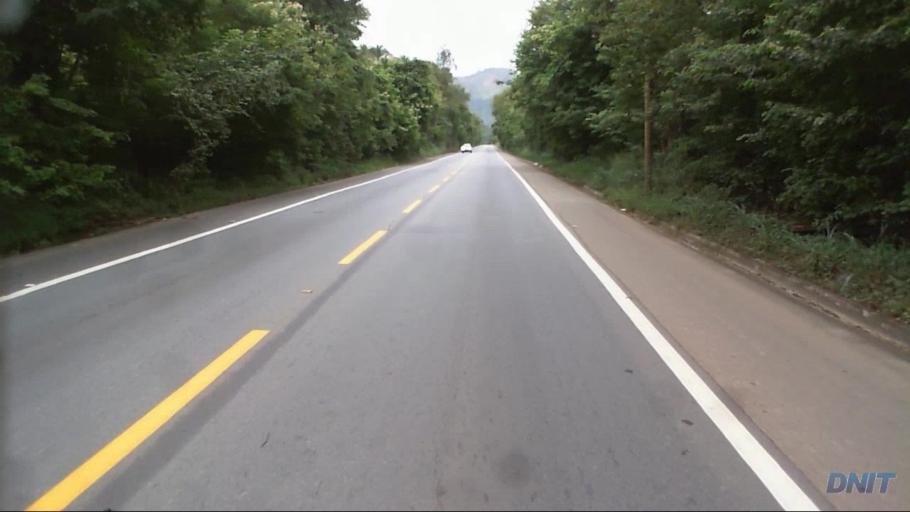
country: BR
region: Minas Gerais
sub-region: Timoteo
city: Timoteo
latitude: -19.5505
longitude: -42.7032
